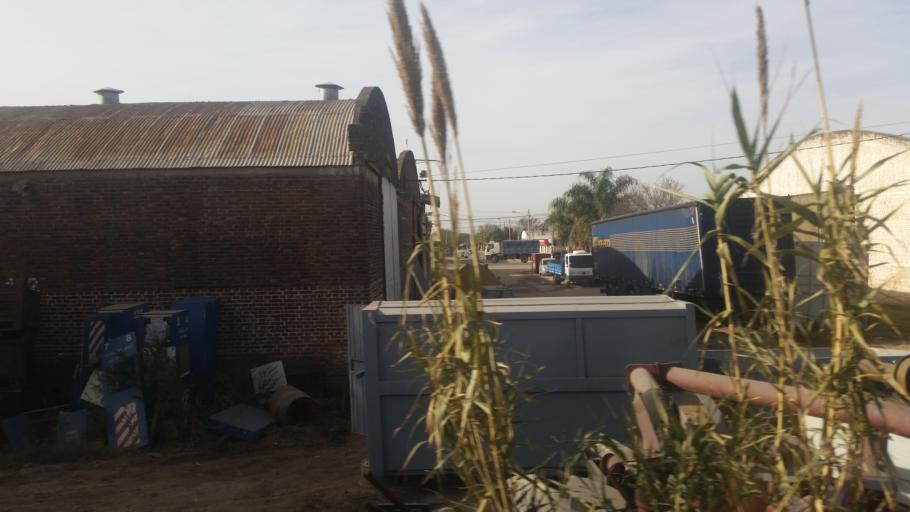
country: AR
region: Cordoba
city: Laguna Larga
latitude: -31.7817
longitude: -63.7989
